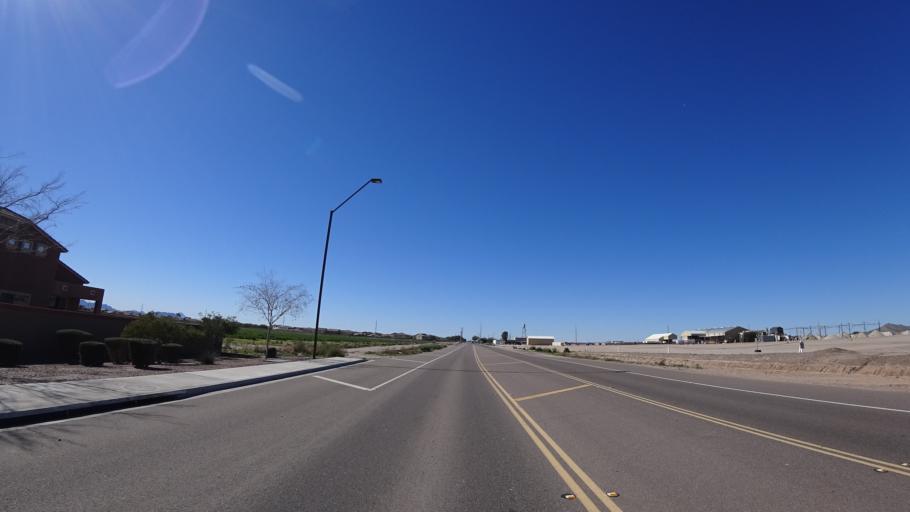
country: US
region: Arizona
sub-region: Maricopa County
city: Buckeye
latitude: 33.3919
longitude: -112.5951
